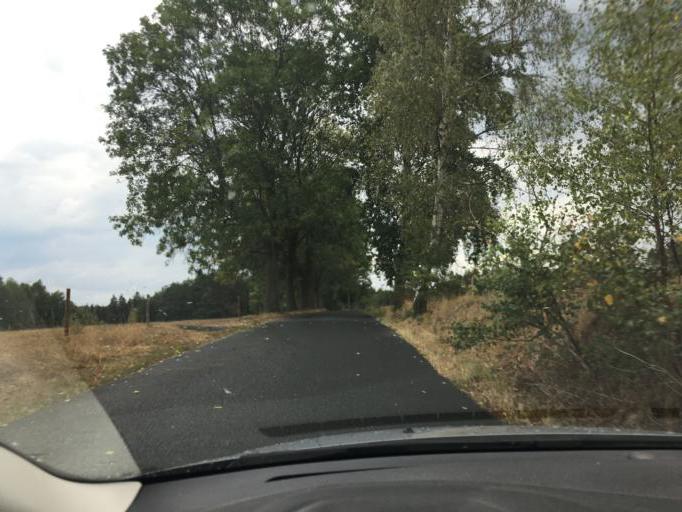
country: CZ
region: Ustecky
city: Benesov nad Ploucnici
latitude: 50.8170
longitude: 14.3373
